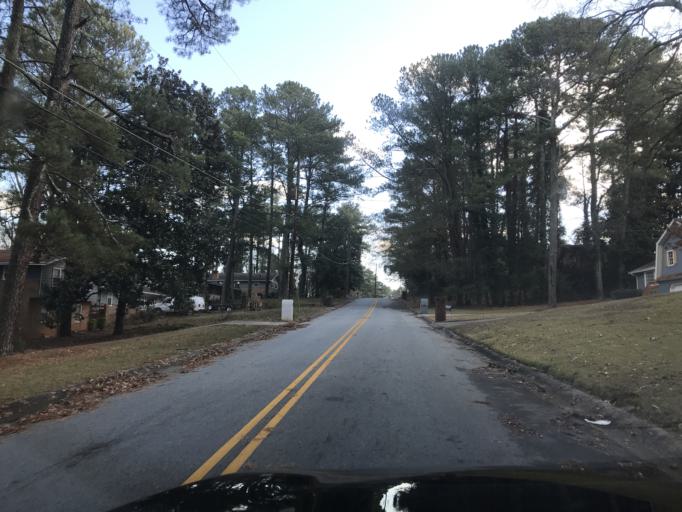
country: US
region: Georgia
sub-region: Fulton County
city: College Park
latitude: 33.6411
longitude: -84.4741
